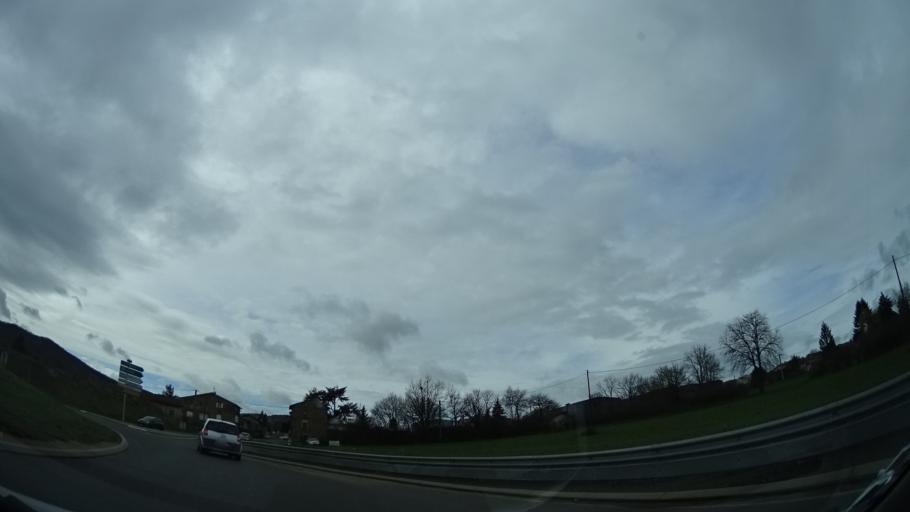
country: FR
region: Rhone-Alpes
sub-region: Departement du Rhone
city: Pontcharra-sur-Turdine
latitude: 45.8777
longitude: 4.5196
